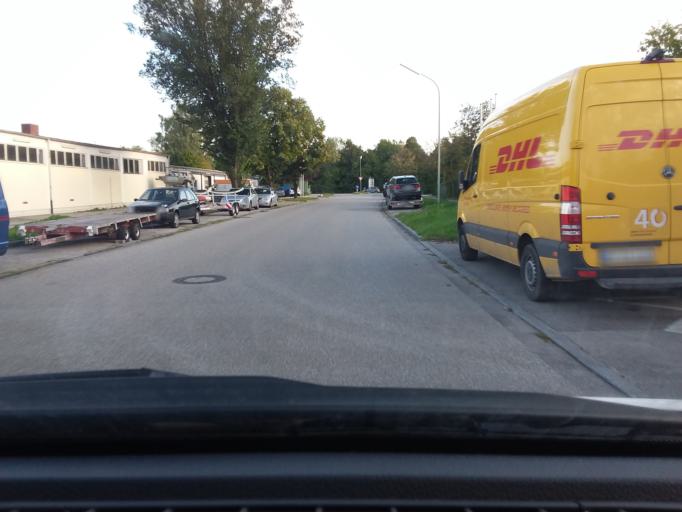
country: DE
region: Bavaria
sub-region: Upper Bavaria
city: Oberschleissheim
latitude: 48.2514
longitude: 11.6071
